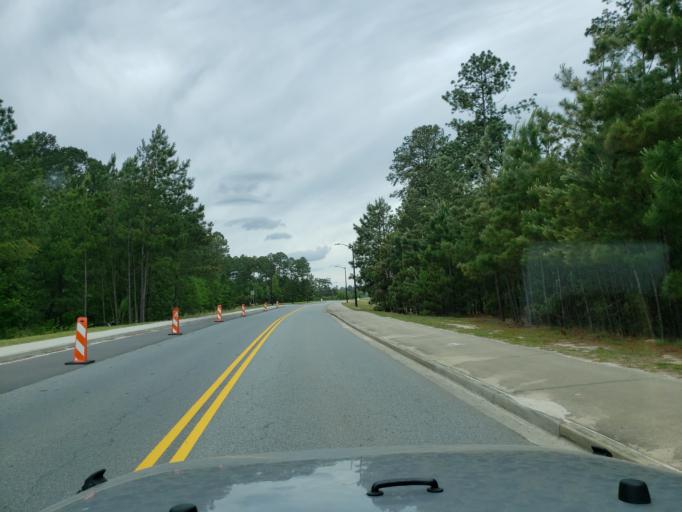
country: US
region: Georgia
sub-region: Chatham County
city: Pooler
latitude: 32.1730
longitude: -81.2255
